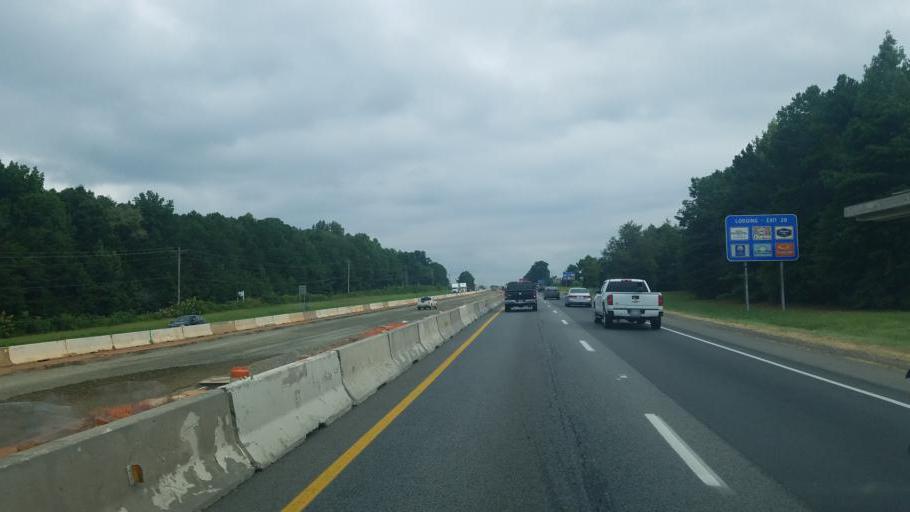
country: US
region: North Carolina
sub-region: Mecklenburg County
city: Cornelius
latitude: 35.4715
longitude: -80.8749
